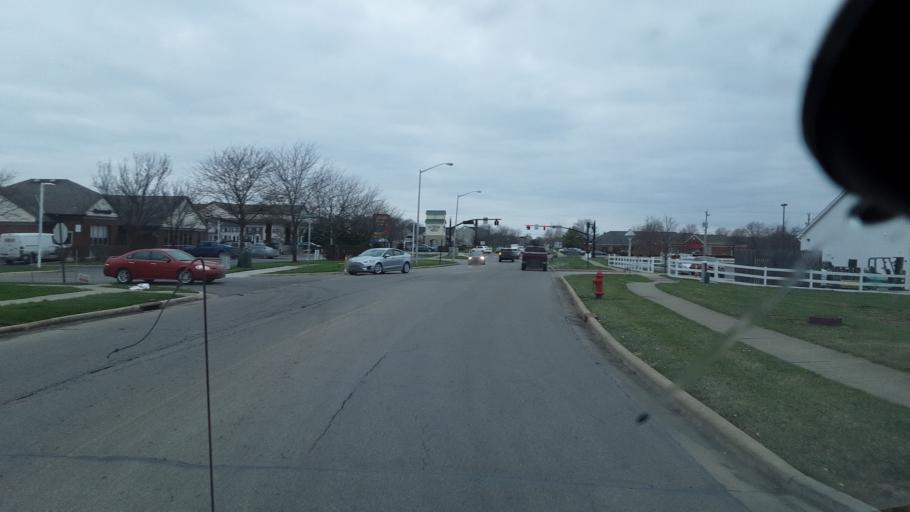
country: US
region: Ohio
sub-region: Delaware County
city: Sunbury
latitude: 40.2417
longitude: -82.8668
